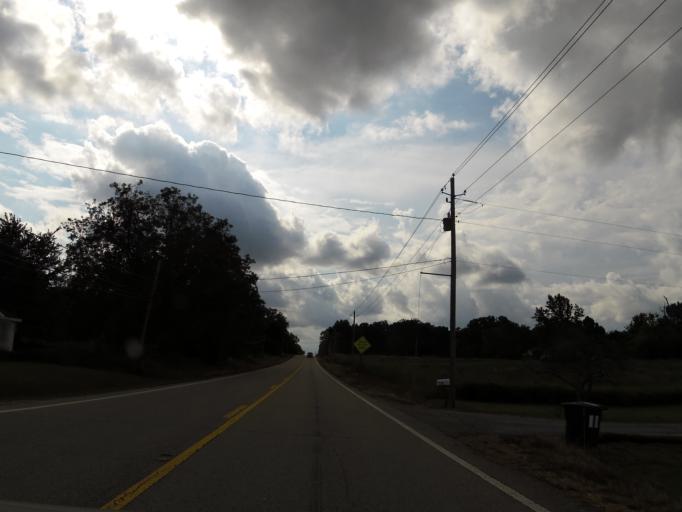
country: US
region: Mississippi
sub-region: Alcorn County
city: Farmington
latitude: 34.9815
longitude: -88.4673
